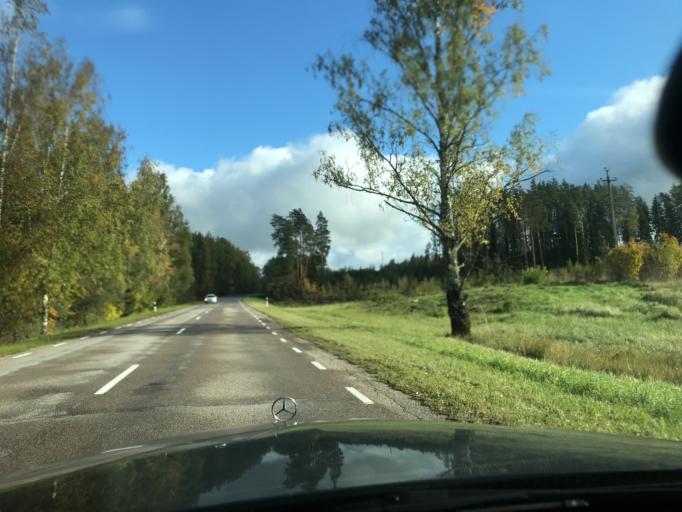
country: EE
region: Valgamaa
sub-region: Torva linn
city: Torva
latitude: 57.9879
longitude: 26.0556
